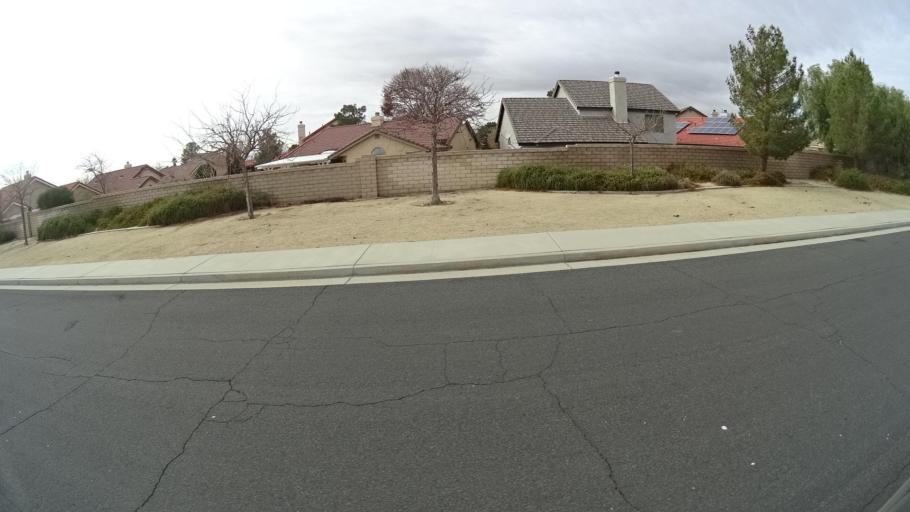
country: US
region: California
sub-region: Kern County
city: Rosamond
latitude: 34.8728
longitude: -118.1495
